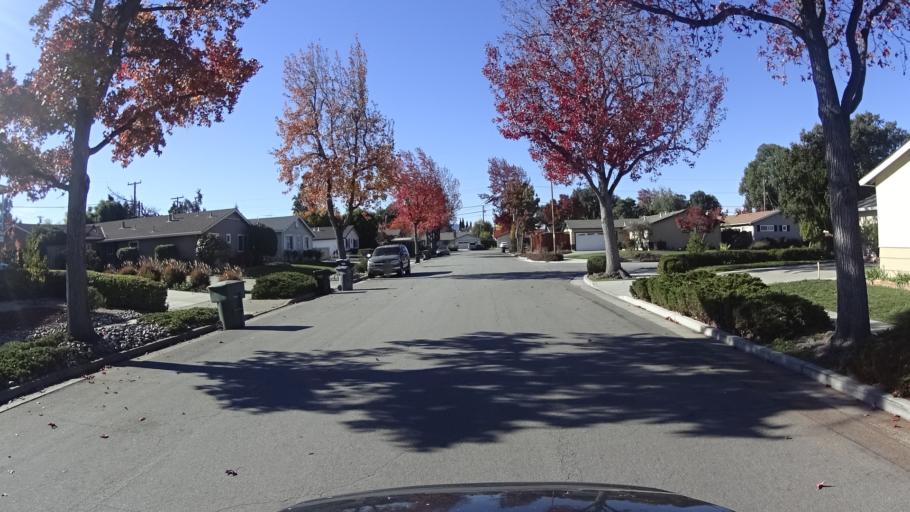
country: US
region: California
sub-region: Santa Clara County
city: Cupertino
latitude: 37.3393
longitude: -122.0111
